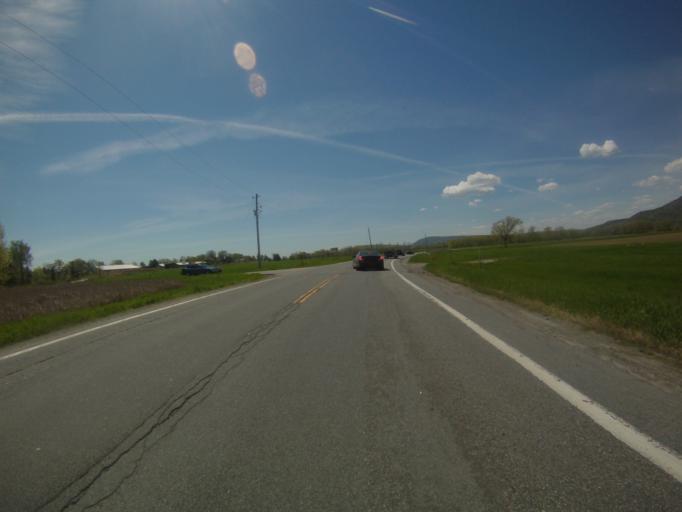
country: US
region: New York
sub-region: Essex County
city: Port Henry
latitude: 44.0023
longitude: -73.4195
